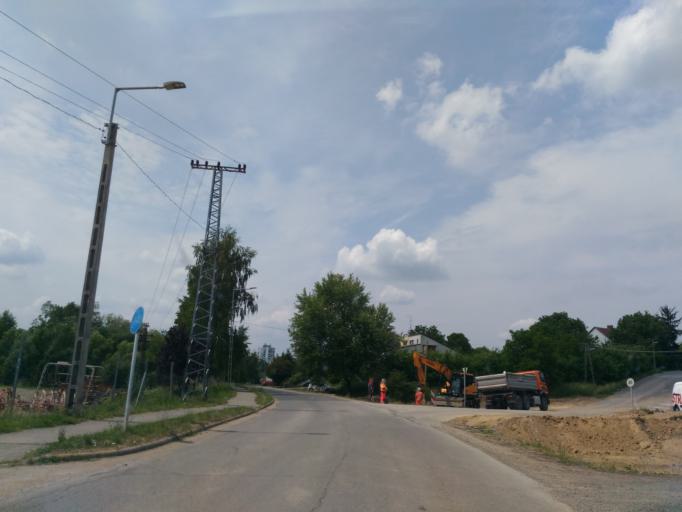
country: HU
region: Baranya
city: Komlo
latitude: 46.1876
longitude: 18.2406
